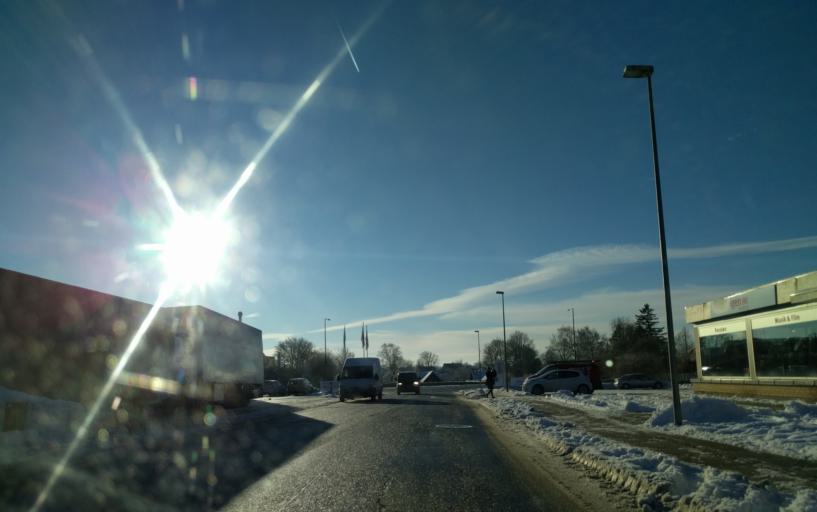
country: DK
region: North Denmark
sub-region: Alborg Kommune
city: Aalborg
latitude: 57.0334
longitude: 9.9228
